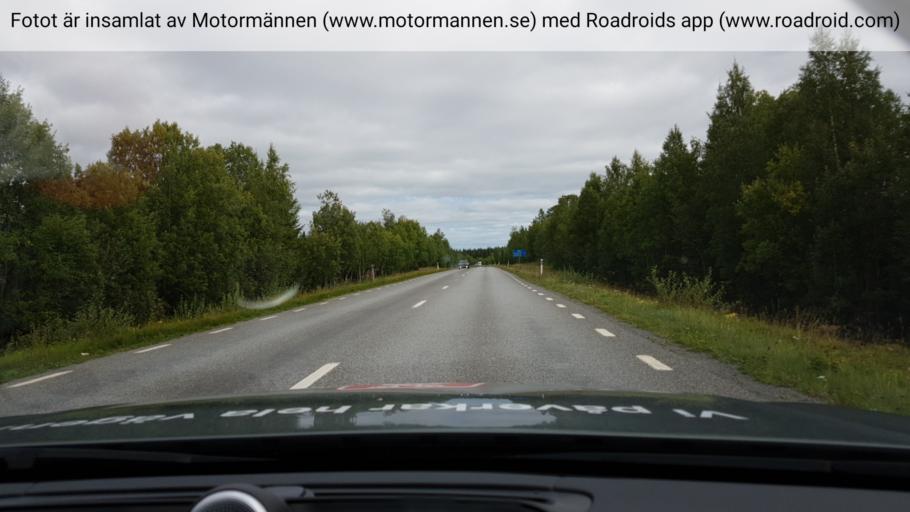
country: SE
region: Jaemtland
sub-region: Stroemsunds Kommun
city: Stroemsund
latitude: 63.5113
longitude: 15.2847
